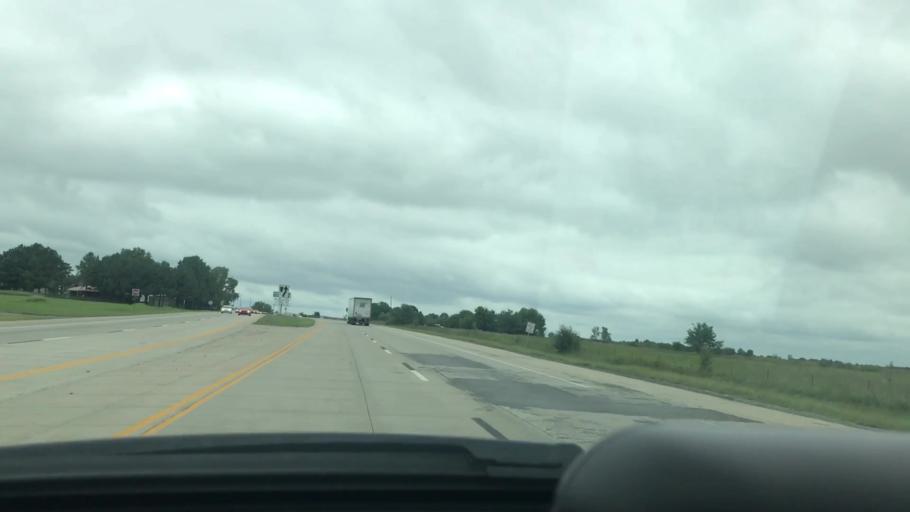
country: US
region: Oklahoma
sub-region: Pittsburg County
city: McAlester
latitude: 34.7292
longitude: -95.8985
